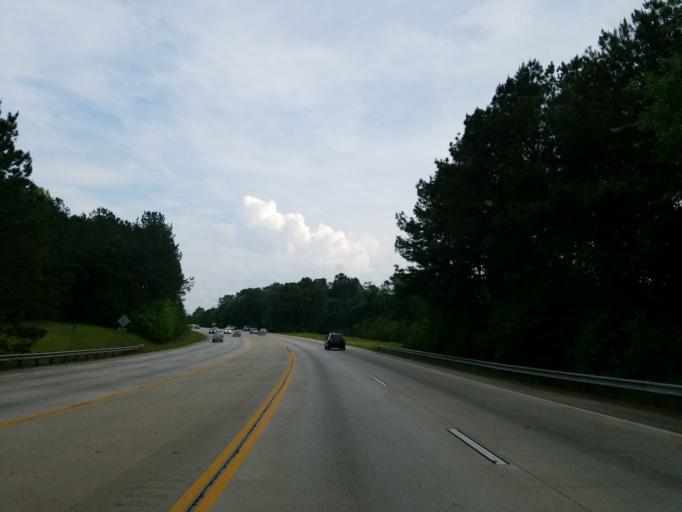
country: US
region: Georgia
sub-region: Cobb County
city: Powder Springs
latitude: 33.8523
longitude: -84.6976
